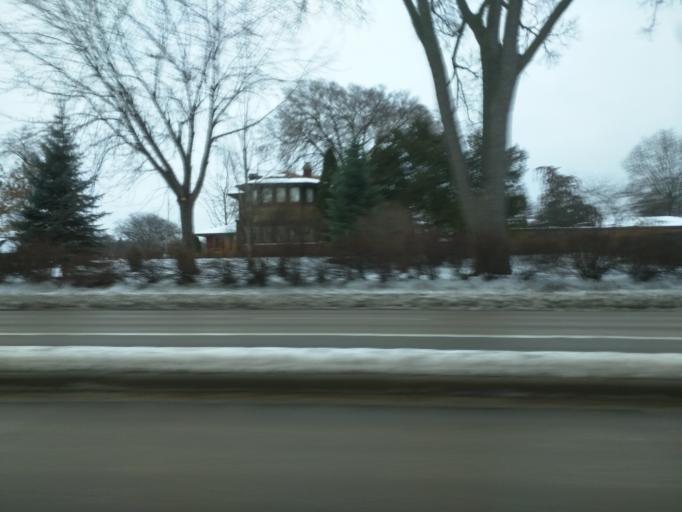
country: US
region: Wisconsin
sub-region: La Crosse County
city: La Crosse
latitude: 43.8084
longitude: -91.2392
